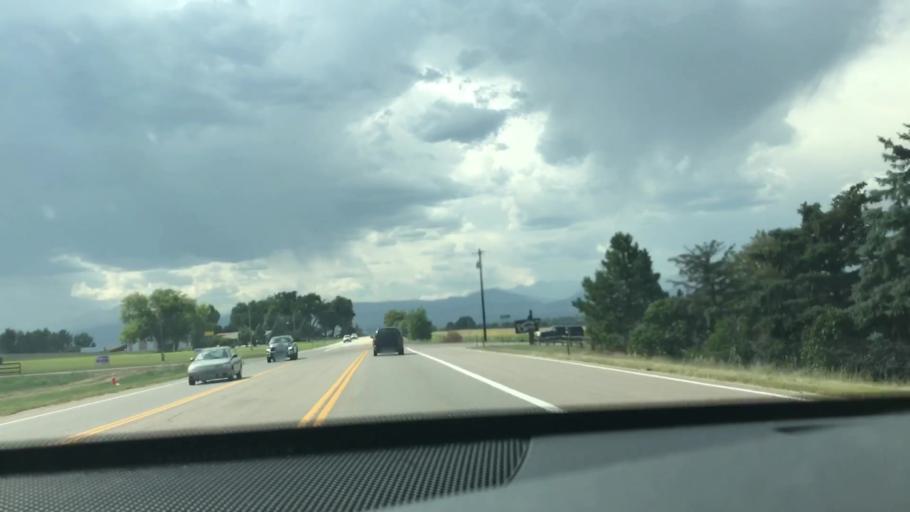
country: US
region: Colorado
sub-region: Larimer County
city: Loveland
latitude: 40.3791
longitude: -105.0117
